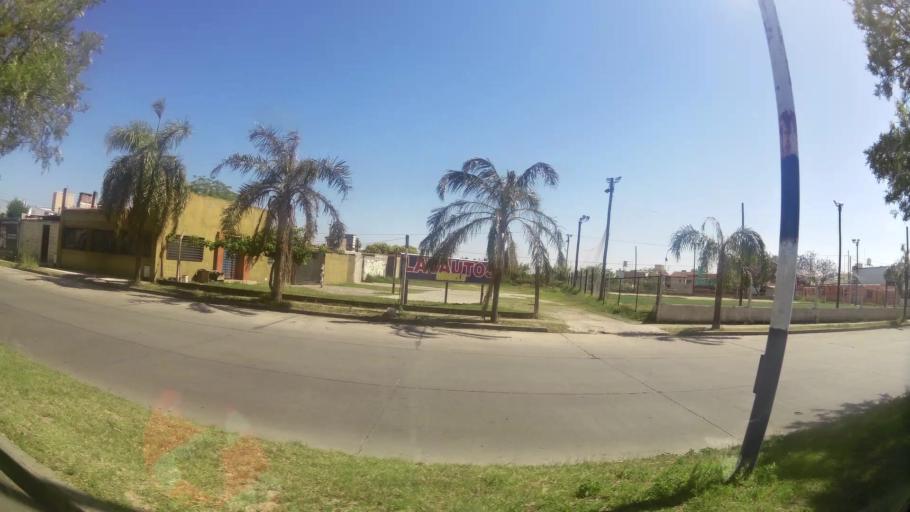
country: AR
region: Cordoba
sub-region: Departamento de Capital
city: Cordoba
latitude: -31.4198
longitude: -64.2178
